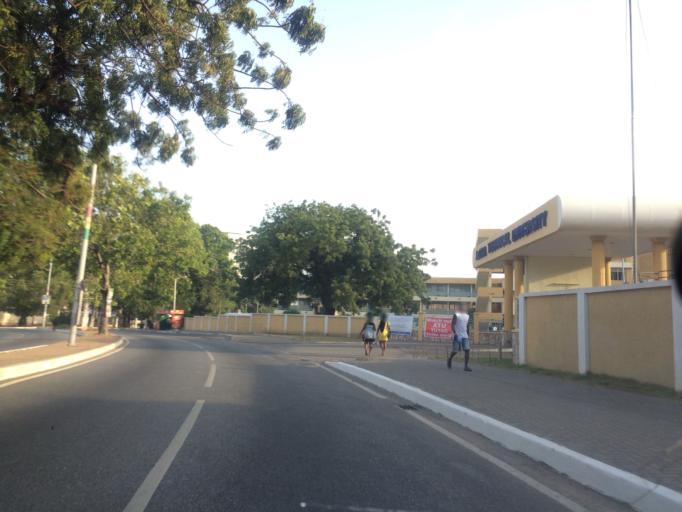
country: GH
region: Greater Accra
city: Accra
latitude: 5.5546
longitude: -0.2052
